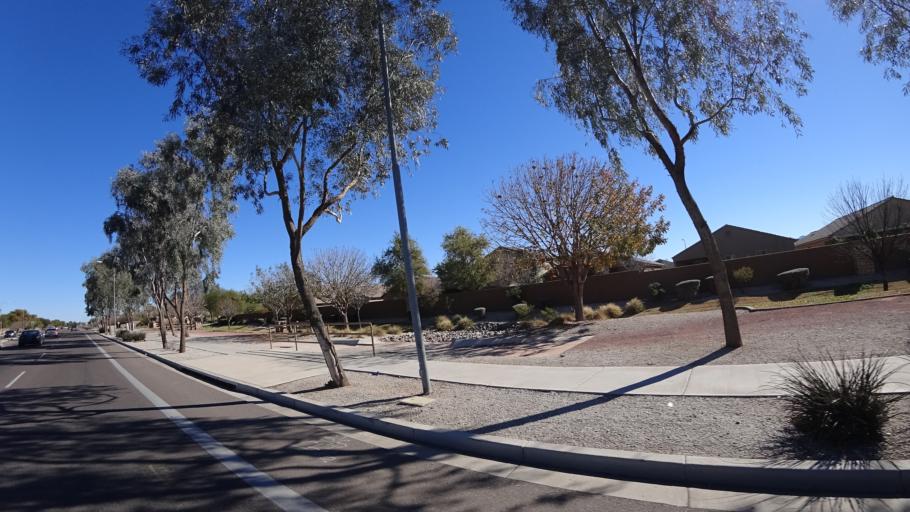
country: US
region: Arizona
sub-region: Maricopa County
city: Tolleson
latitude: 33.4218
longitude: -112.2486
